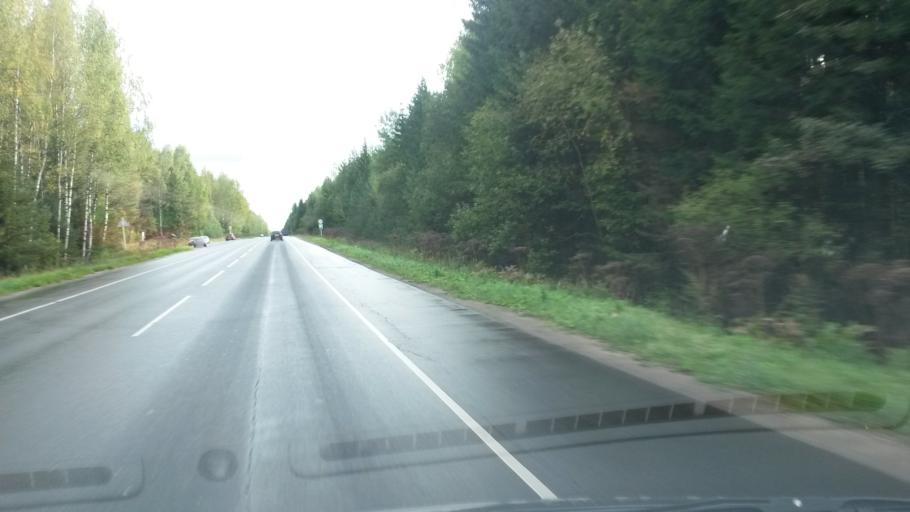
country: RU
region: Ivanovo
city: Kaminskiy
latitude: 57.0410
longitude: 41.3385
